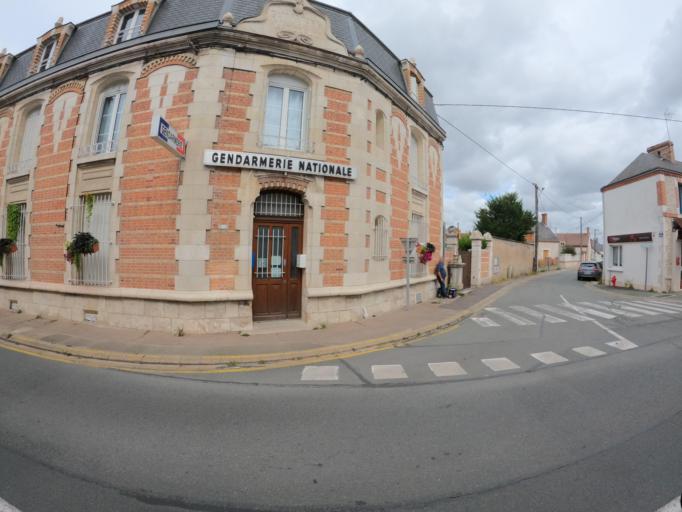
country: FR
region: Centre
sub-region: Departement du Loiret
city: Clery-Saint-Andre
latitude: 47.8232
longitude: 1.7570
